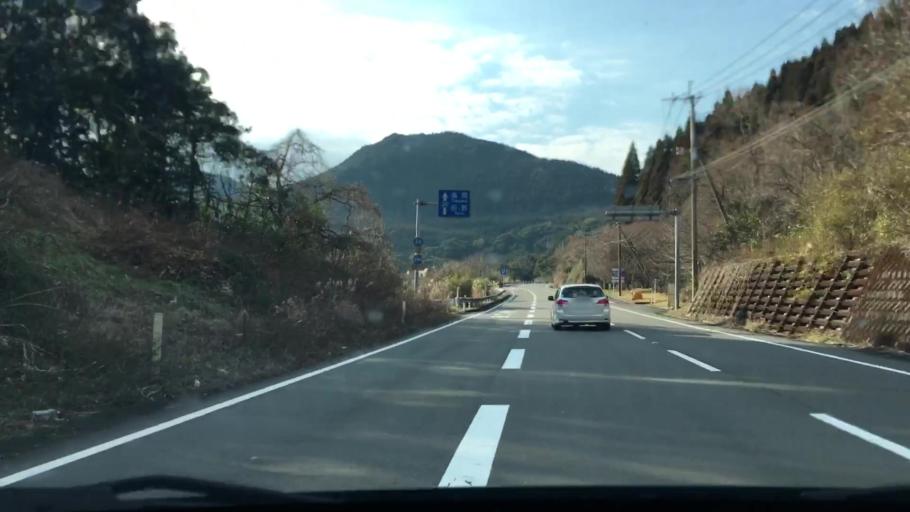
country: JP
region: Miyazaki
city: Miyazaki-shi
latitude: 31.7798
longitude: 131.3281
